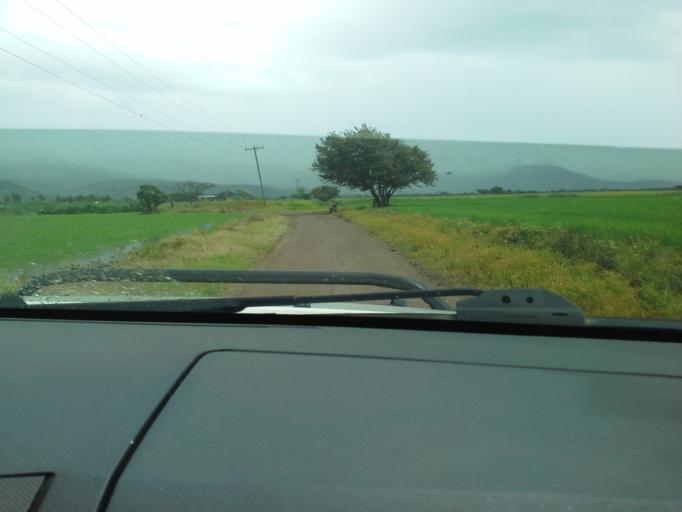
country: NI
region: Matagalpa
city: Ciudad Dario
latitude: 12.8508
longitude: -86.1783
